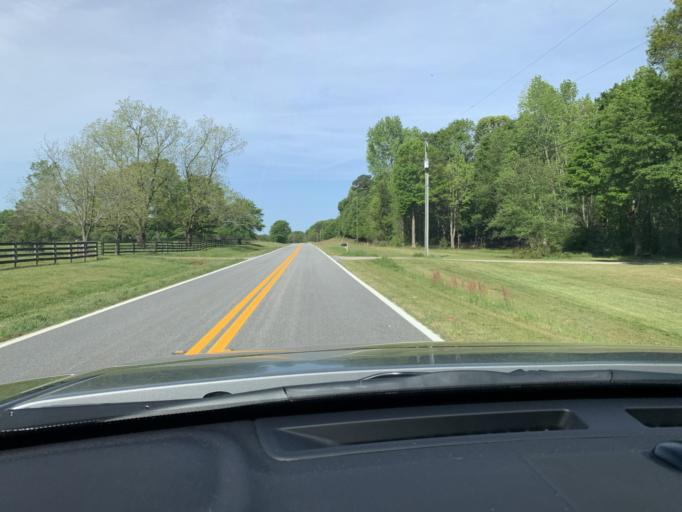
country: US
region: Georgia
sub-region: Oconee County
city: Watkinsville
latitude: 33.8158
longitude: -83.3885
